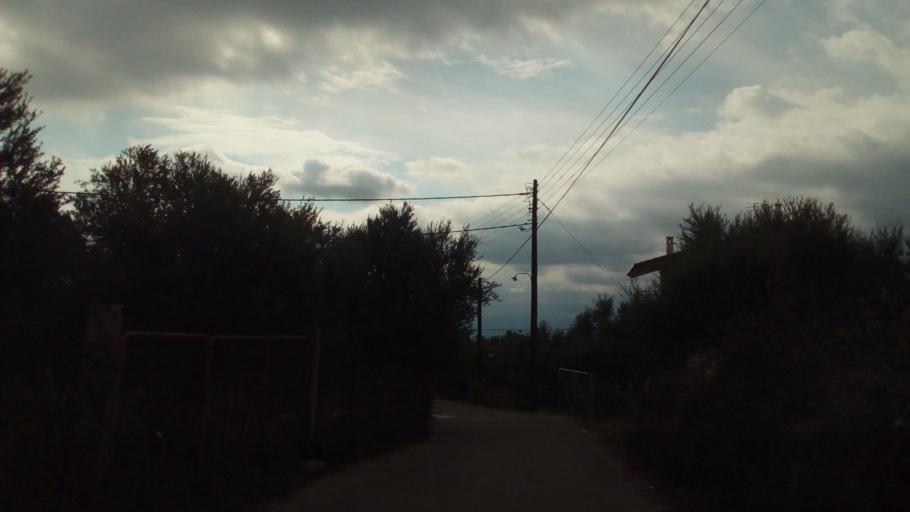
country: GR
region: West Greece
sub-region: Nomos Achaias
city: Kamarai
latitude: 38.3936
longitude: 22.0101
